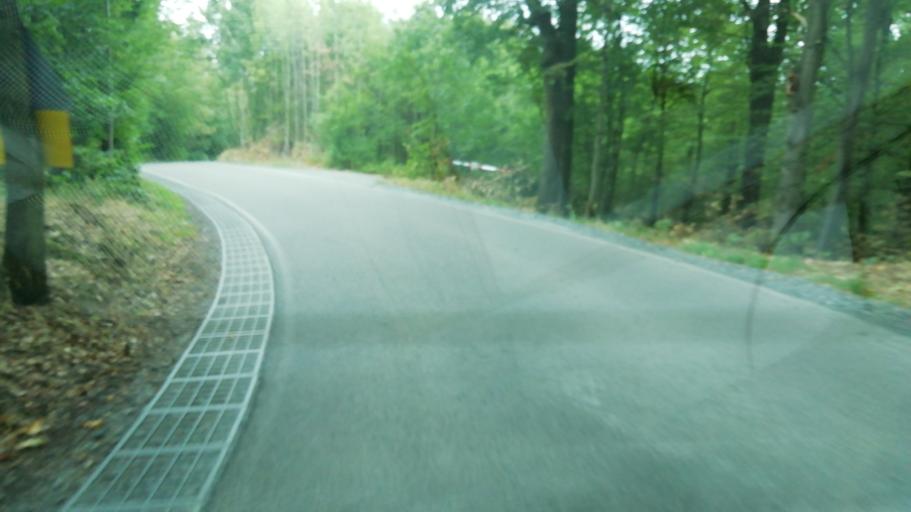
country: DE
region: Saxony
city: Coswig
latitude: 51.0871
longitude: 13.6044
